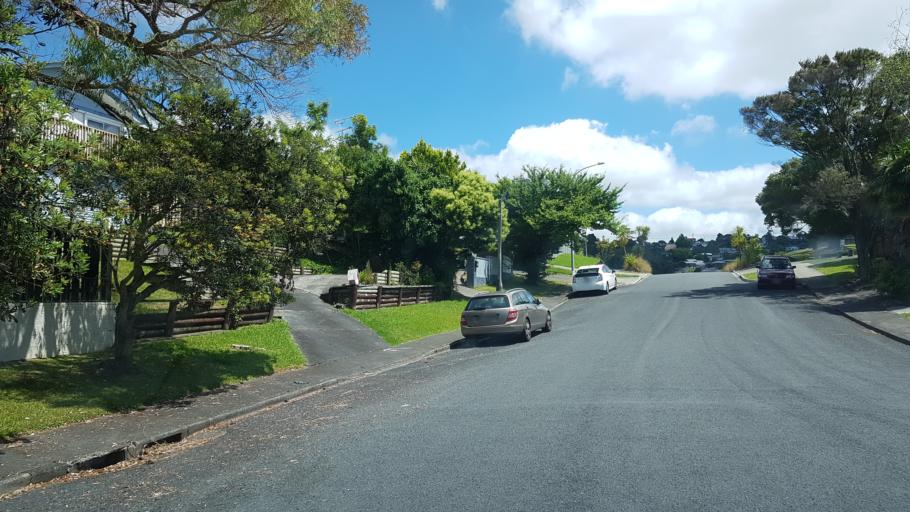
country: NZ
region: Auckland
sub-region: Auckland
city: North Shore
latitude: -36.7858
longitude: 174.7105
